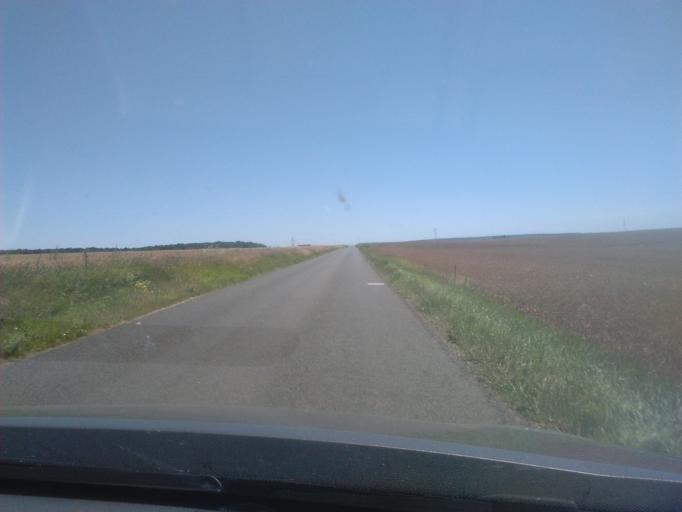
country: FR
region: Centre
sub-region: Departement du Loir-et-Cher
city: Herbault
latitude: 47.6399
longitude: 1.1980
